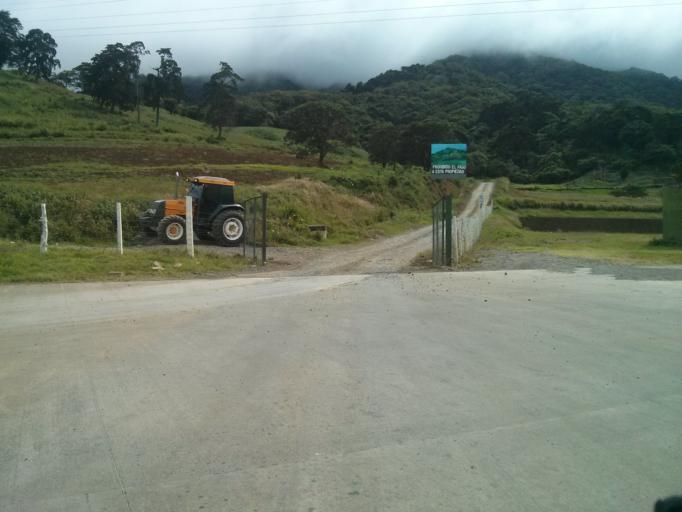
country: CR
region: Cartago
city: Tres Rios
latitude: 9.9001
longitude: -83.9882
